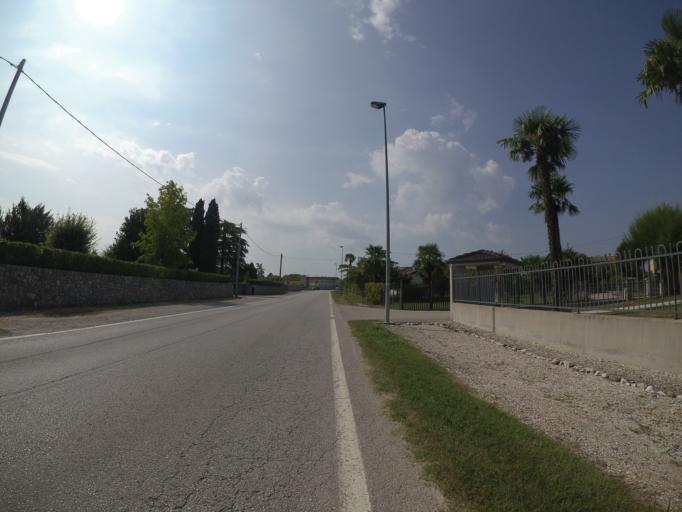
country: IT
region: Friuli Venezia Giulia
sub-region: Provincia di Udine
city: Pocenia
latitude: 45.8227
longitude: 13.0820
